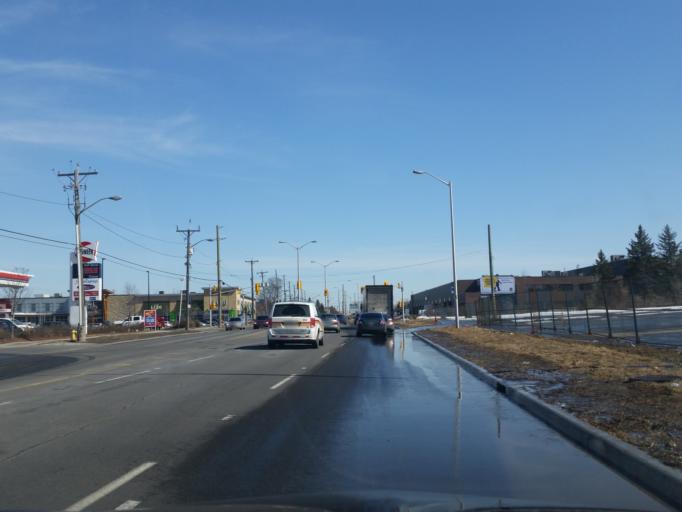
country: CA
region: Ontario
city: Ottawa
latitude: 45.4109
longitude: -75.6419
